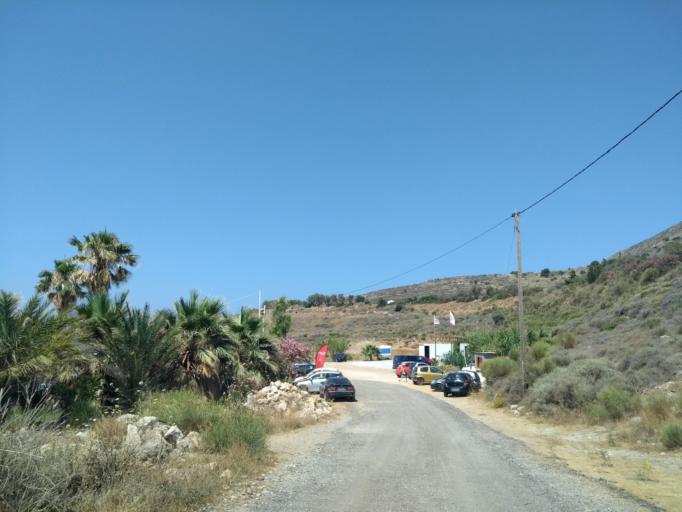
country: GR
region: Crete
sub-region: Nomos Rethymnis
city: Atsipopoulon
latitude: 35.3568
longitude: 24.3694
